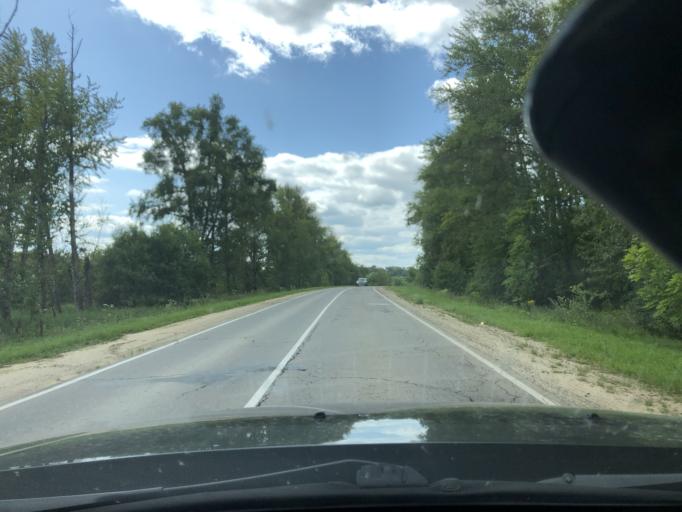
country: RU
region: Tula
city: Revyakino
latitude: 54.3492
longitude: 37.6224
